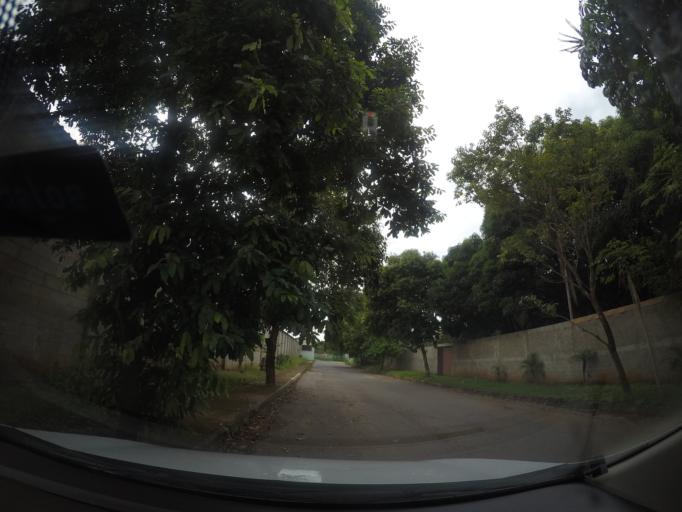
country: BR
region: Goias
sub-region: Goiania
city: Goiania
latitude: -16.6553
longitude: -49.2384
